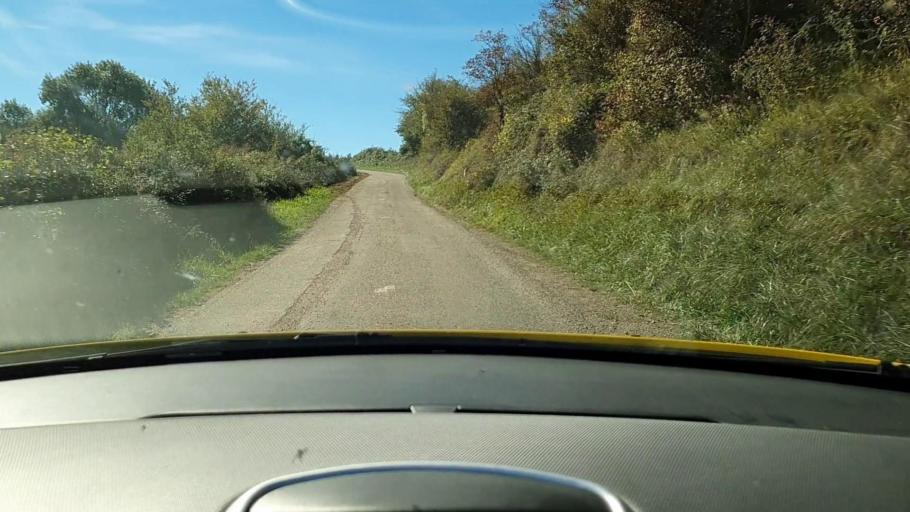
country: FR
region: Languedoc-Roussillon
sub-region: Departement du Gard
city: Aveze
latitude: 43.9612
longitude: 3.4259
